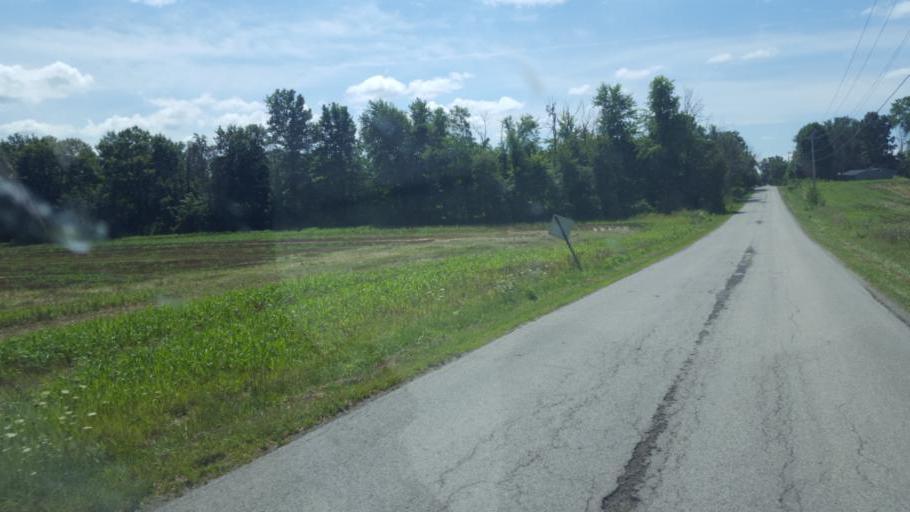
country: US
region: Ohio
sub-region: Knox County
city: Centerburg
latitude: 40.3857
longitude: -82.7898
